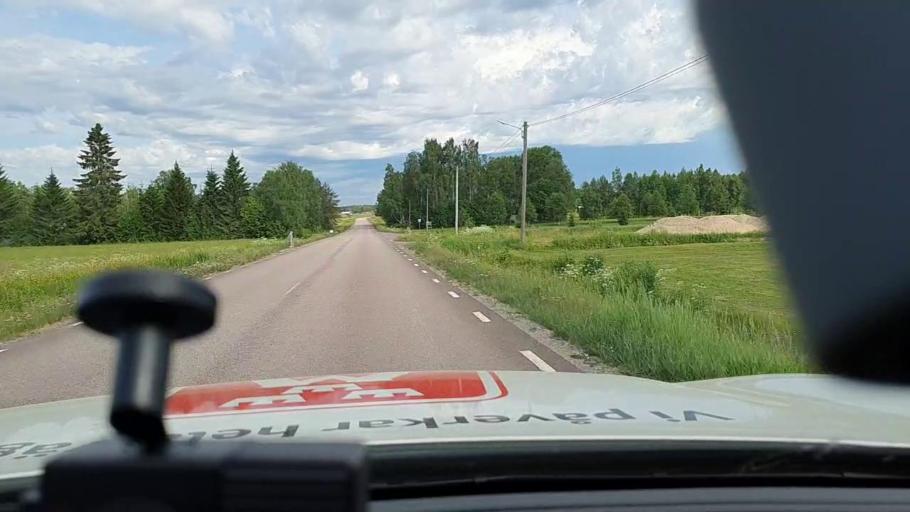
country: SE
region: Norrbotten
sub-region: Bodens Kommun
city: Saevast
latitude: 65.6957
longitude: 21.7787
